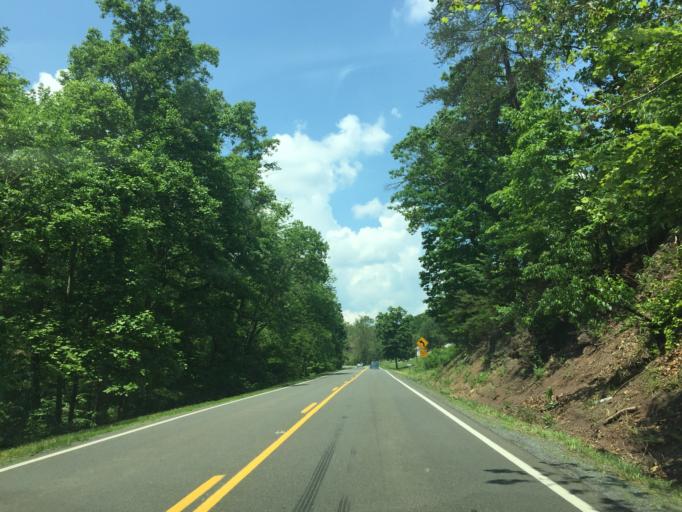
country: US
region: Virginia
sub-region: Shenandoah County
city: Strasburg
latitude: 39.0796
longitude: -78.3817
